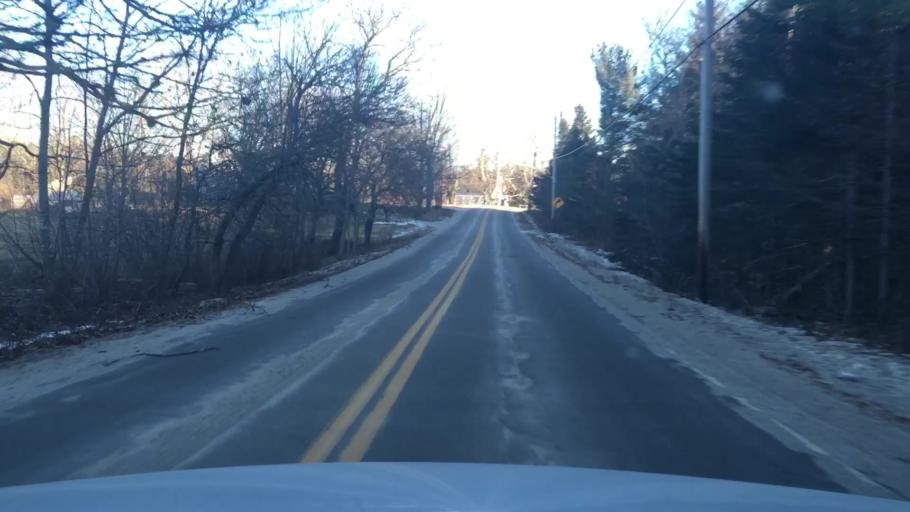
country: US
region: Maine
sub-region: Hancock County
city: Penobscot
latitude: 44.3894
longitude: -68.7012
